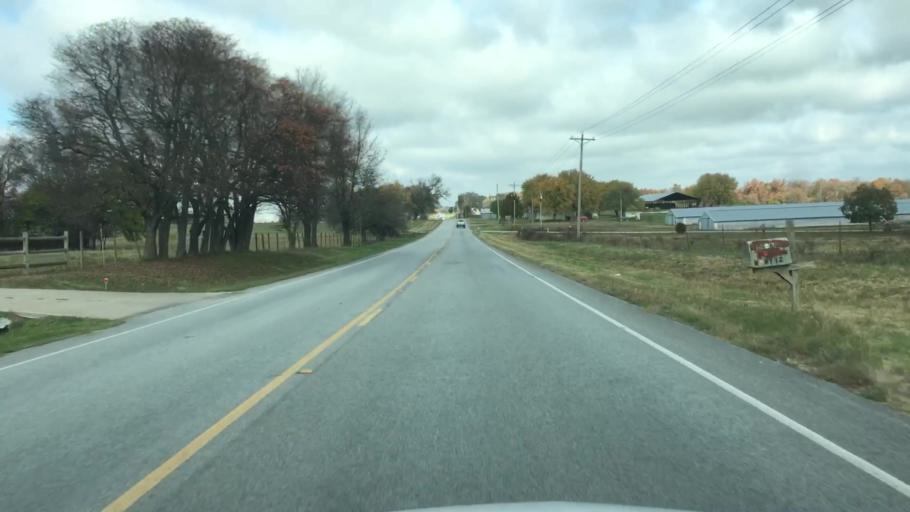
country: US
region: Arkansas
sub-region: Benton County
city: Centerton
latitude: 36.2709
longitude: -94.3503
